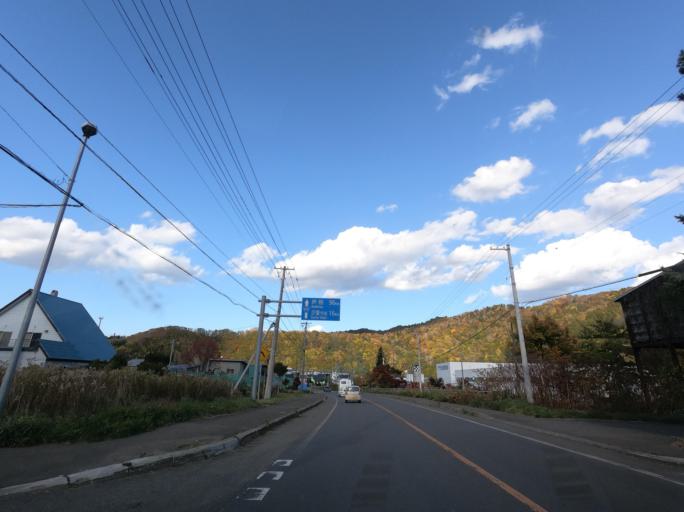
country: JP
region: Hokkaido
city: Iwamizawa
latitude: 42.9401
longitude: 142.0422
